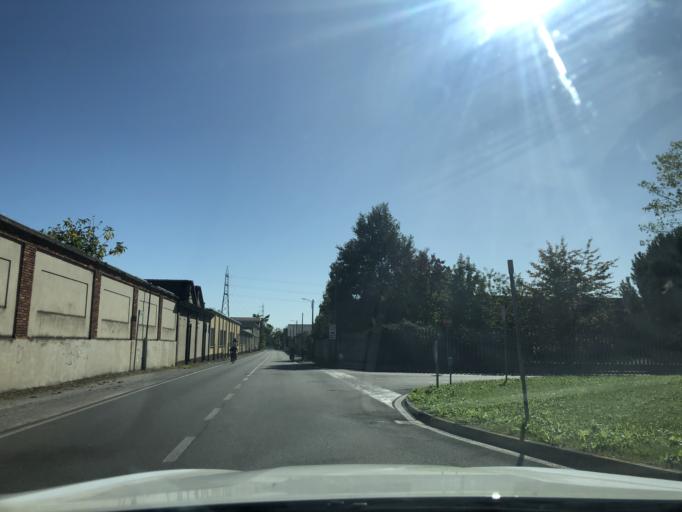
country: IT
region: Lombardy
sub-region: Provincia di Monza e Brianza
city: Villaggio del Sole
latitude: 45.6318
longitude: 9.1172
